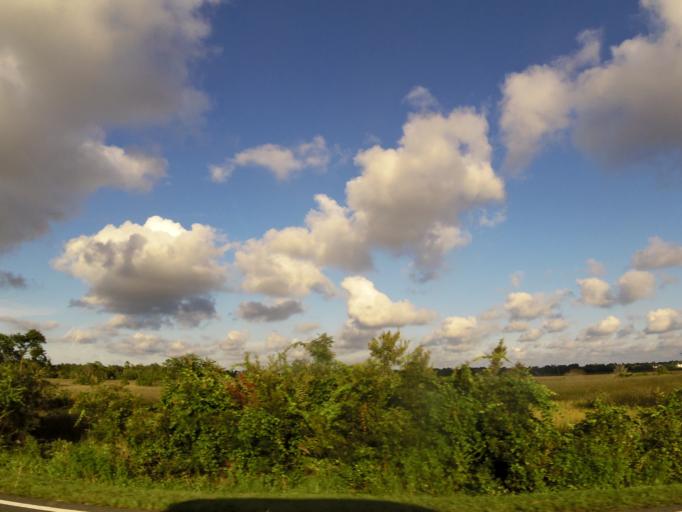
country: US
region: Georgia
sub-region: Glynn County
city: Saint Simon Mills
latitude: 31.1832
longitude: -81.3993
